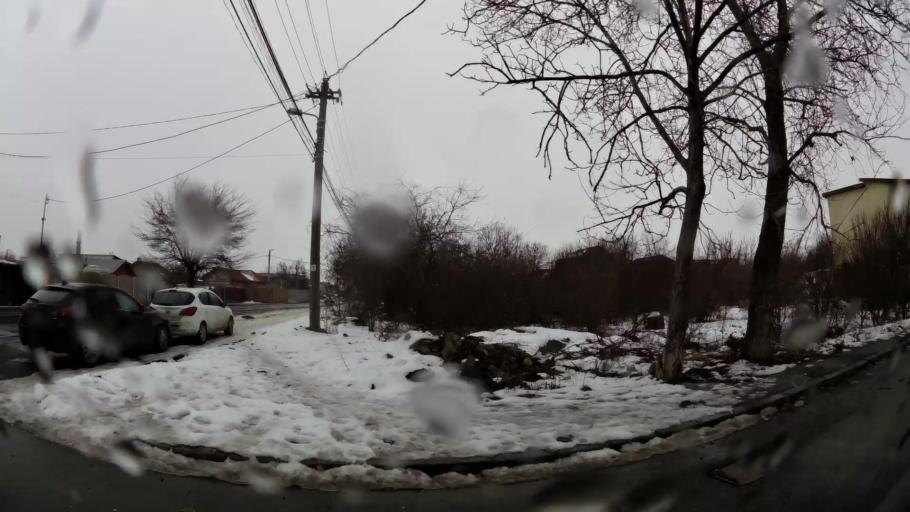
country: RO
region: Ilfov
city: Dobroesti
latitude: 44.4221
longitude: 26.1839
